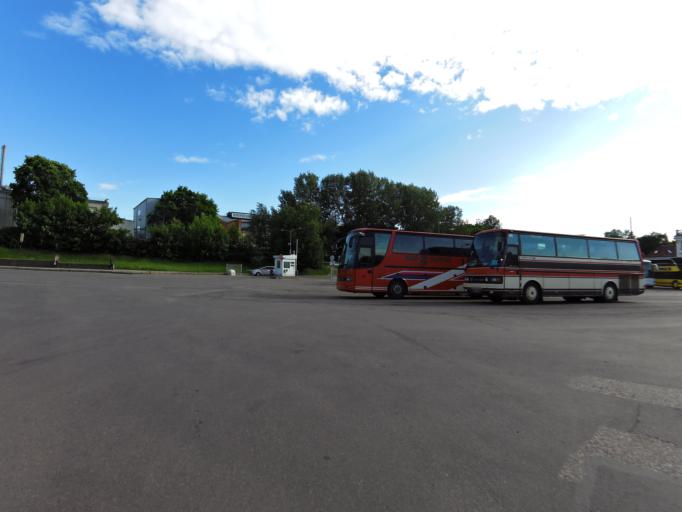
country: LT
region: Vilnius County
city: Naujamiestis
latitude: 54.6703
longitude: 25.2799
